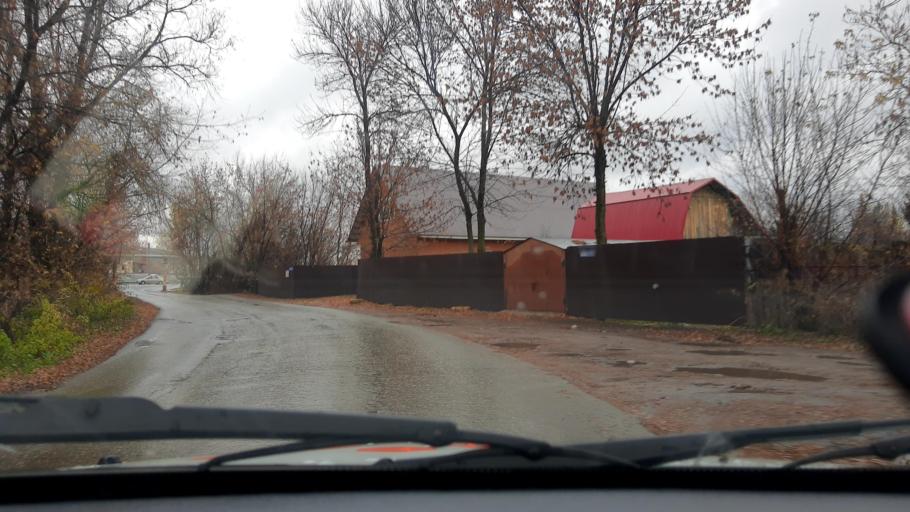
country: RU
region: Bashkortostan
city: Ufa
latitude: 54.8048
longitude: 56.1512
